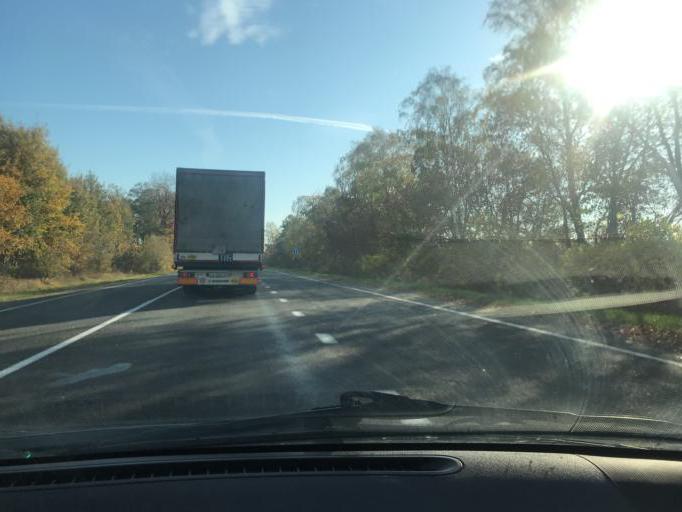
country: BY
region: Brest
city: Ivanava
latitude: 52.1476
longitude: 25.4326
